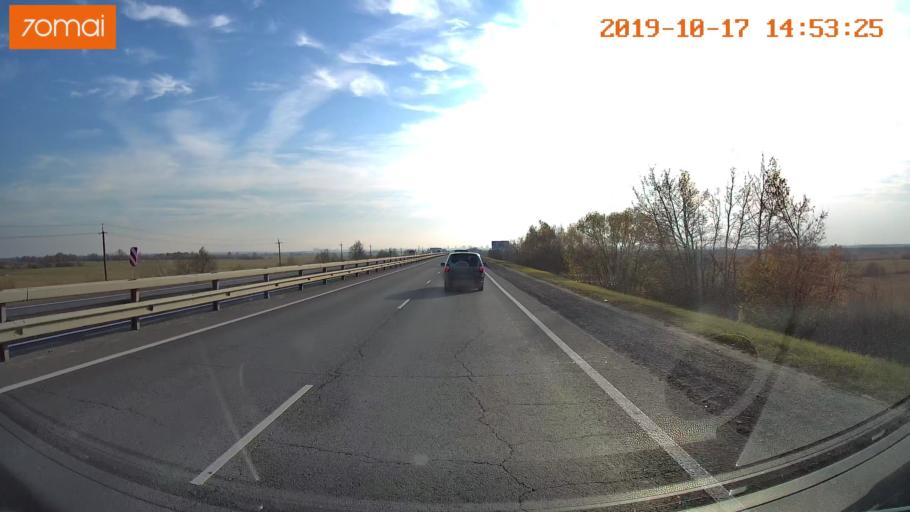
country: RU
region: Rjazan
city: Polyany
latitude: 54.6946
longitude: 39.8386
